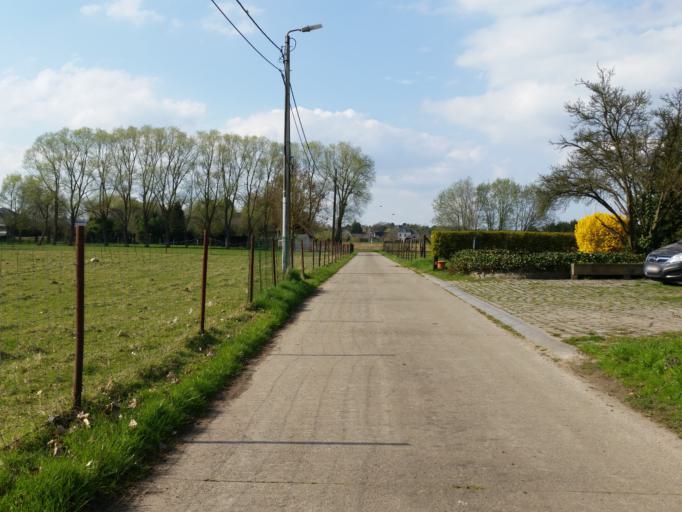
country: BE
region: Flanders
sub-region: Provincie Vlaams-Brabant
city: Kampenhout
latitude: 50.9607
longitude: 4.5147
